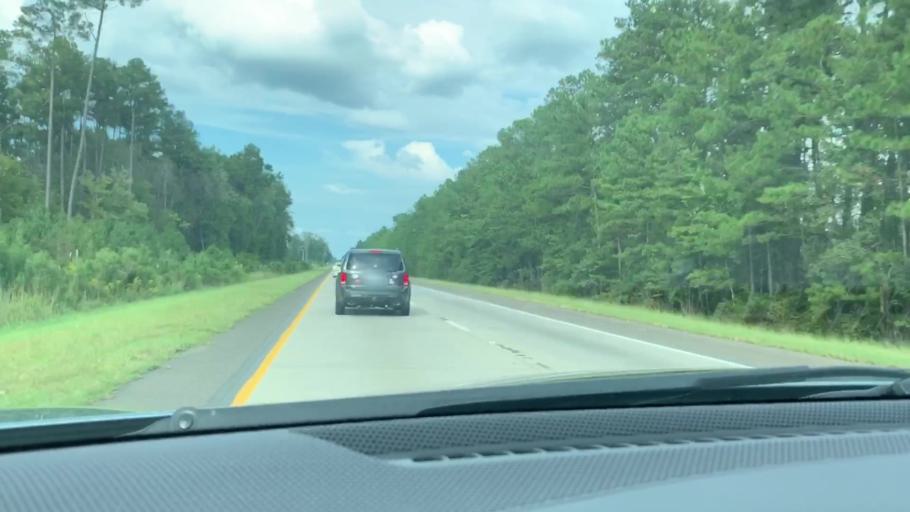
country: US
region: South Carolina
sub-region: Colleton County
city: Walterboro
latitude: 32.8554
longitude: -80.7305
